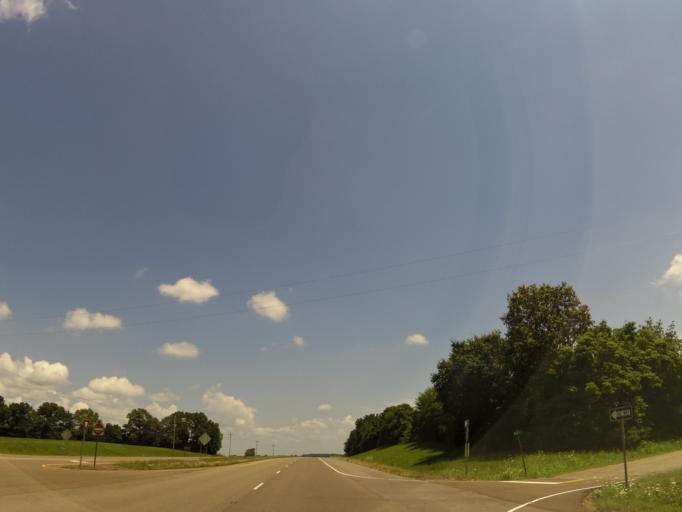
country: US
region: Tennessee
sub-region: Lauderdale County
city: Halls
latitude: 35.8933
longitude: -89.2391
